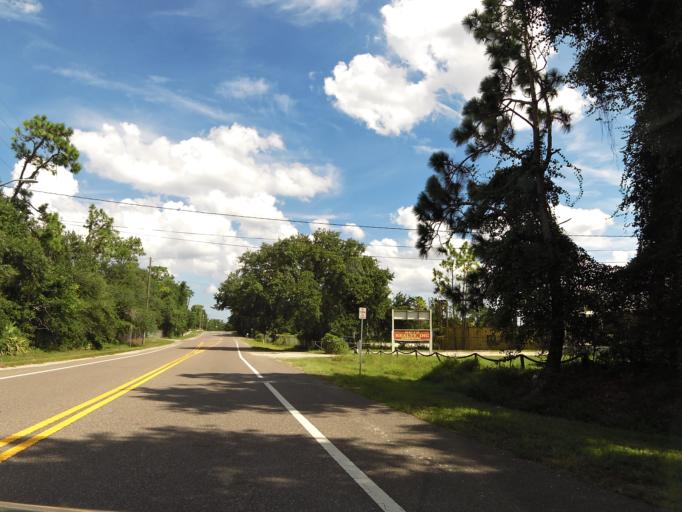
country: US
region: Florida
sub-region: Duval County
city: Jacksonville
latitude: 30.4235
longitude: -81.5741
